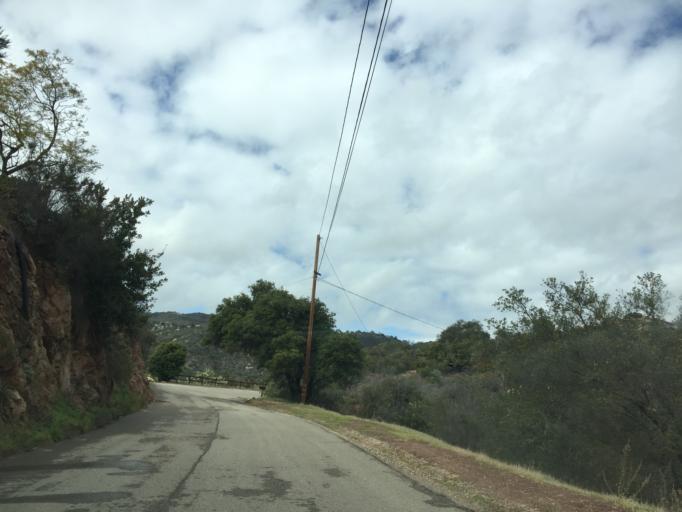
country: US
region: California
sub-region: Santa Barbara County
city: Goleta
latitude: 34.4816
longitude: -119.7974
